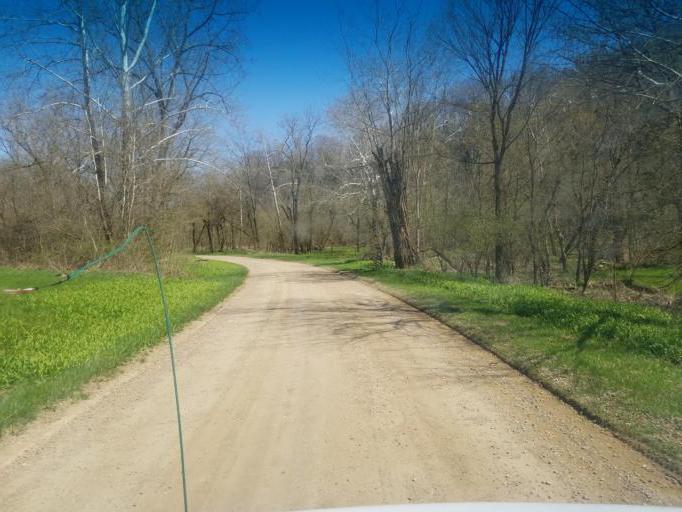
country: US
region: Ohio
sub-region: Knox County
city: Oak Hill
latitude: 40.3786
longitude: -82.2420
